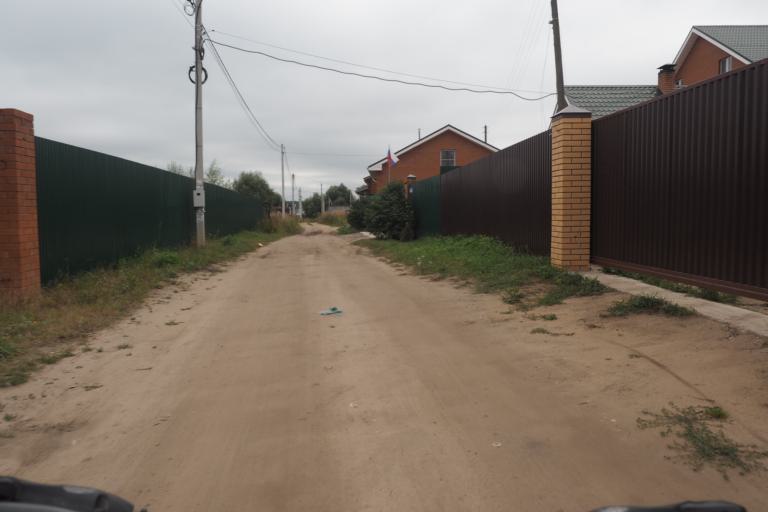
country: RU
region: Moskovskaya
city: Malyshevo
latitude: 55.5367
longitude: 38.3315
